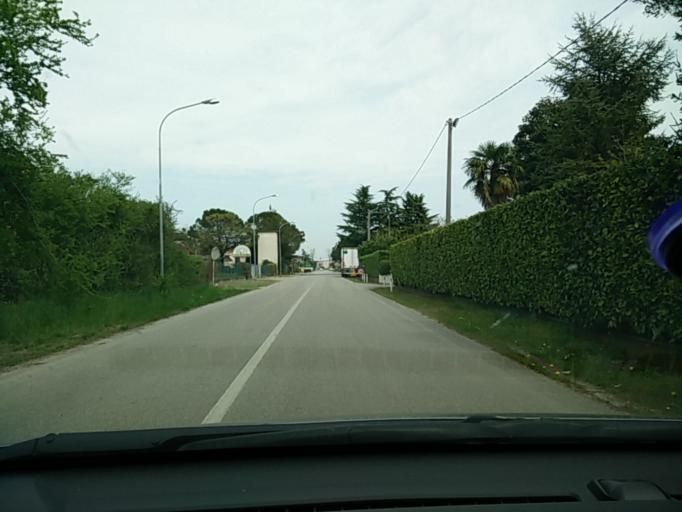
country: IT
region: Veneto
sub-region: Provincia di Venezia
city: Musile di Piave
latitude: 45.6193
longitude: 12.5378
